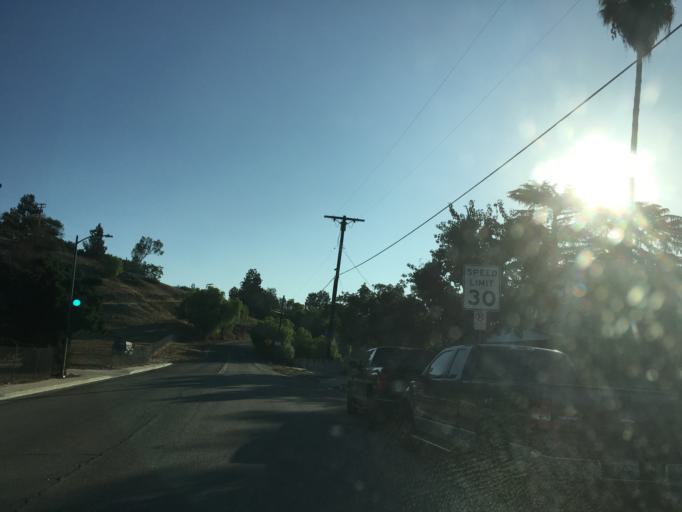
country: US
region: California
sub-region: Los Angeles County
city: San Fernando
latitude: 34.2827
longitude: -118.3777
